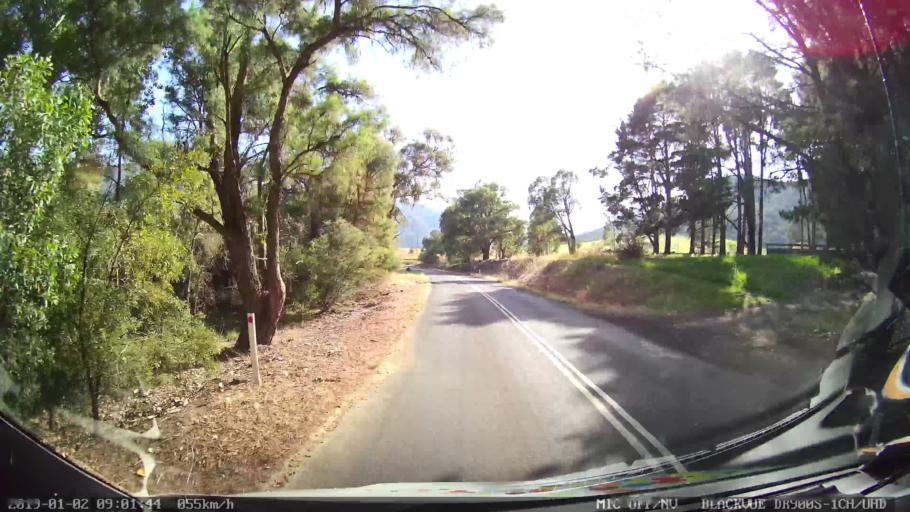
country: AU
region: New South Wales
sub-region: Tumut Shire
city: Tumut
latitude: -35.5780
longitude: 148.3087
